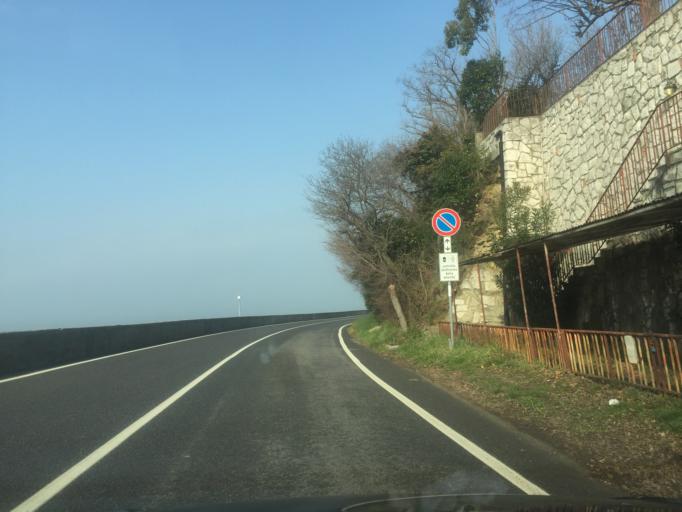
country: SI
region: Koper-Capodistria
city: Ankaran
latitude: 45.6023
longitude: 13.7202
